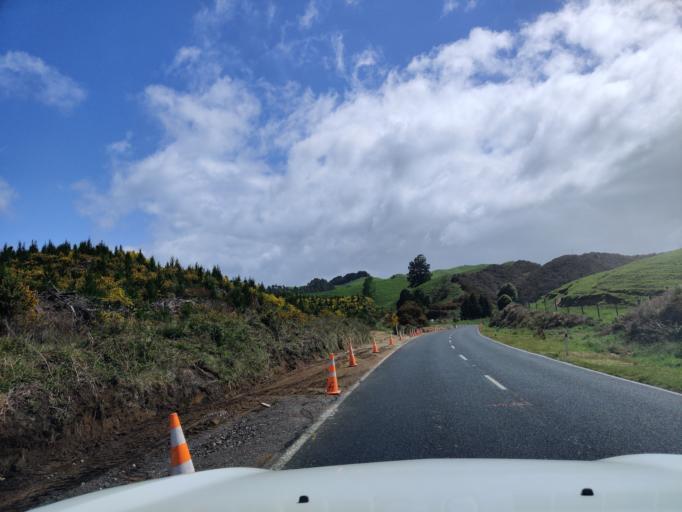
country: NZ
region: Bay of Plenty
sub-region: Rotorua District
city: Rotorua
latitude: -38.1711
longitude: 176.3214
